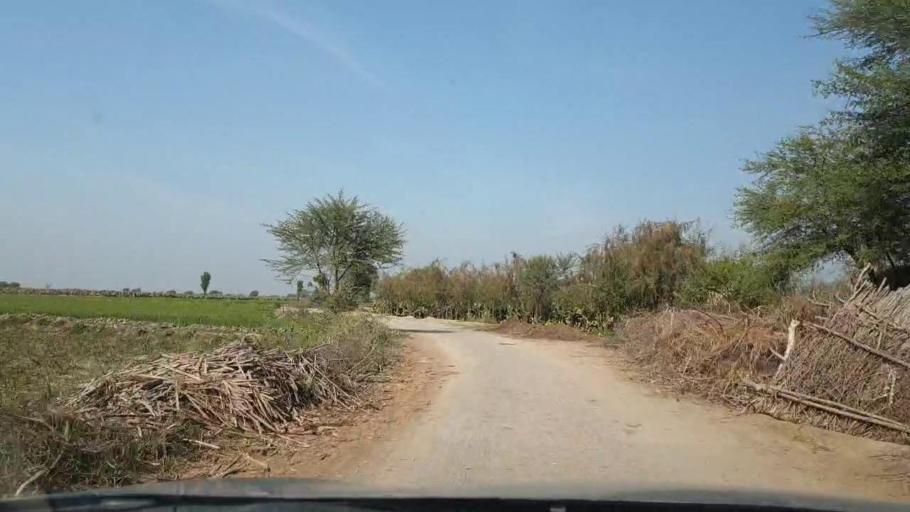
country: PK
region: Sindh
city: Berani
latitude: 25.6990
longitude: 68.7537
